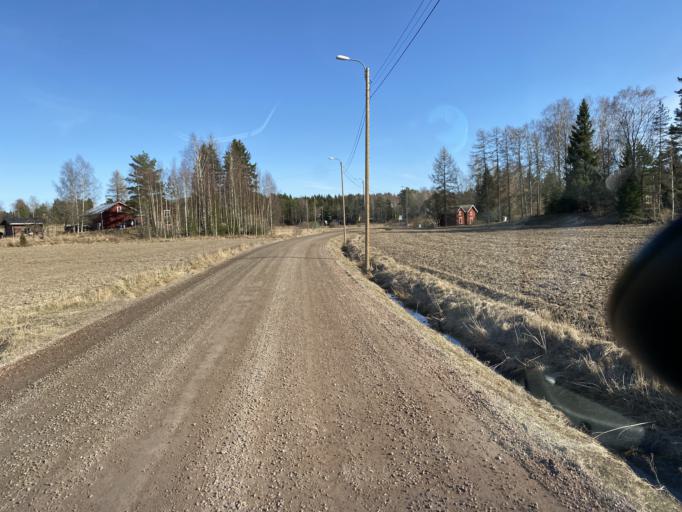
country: FI
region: Satakunta
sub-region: Rauma
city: Lappi
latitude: 61.1397
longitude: 21.9462
